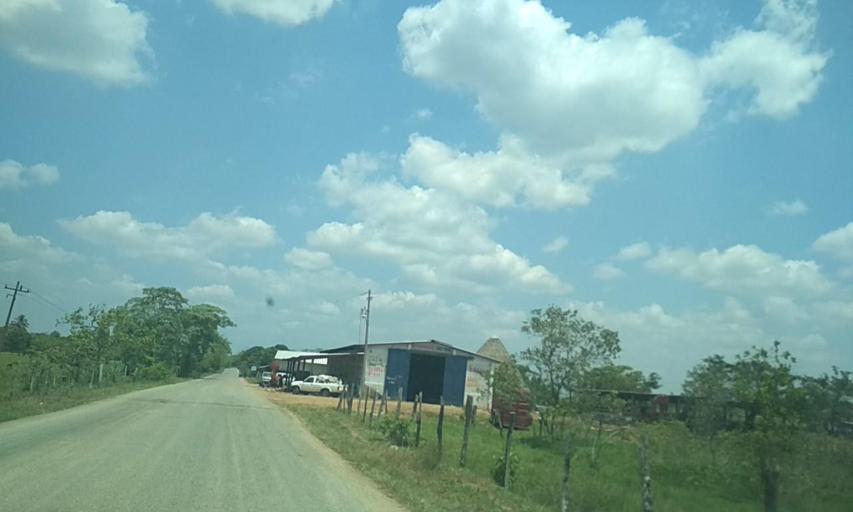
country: MX
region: Tabasco
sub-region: Huimanguillo
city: Francisco Rueda
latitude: 17.7738
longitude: -93.8132
